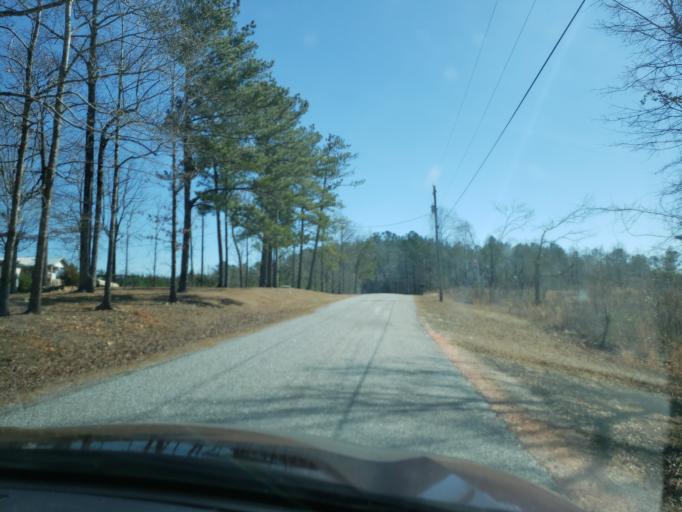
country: US
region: Alabama
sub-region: Elmore County
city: Tallassee
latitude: 32.6636
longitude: -85.8606
